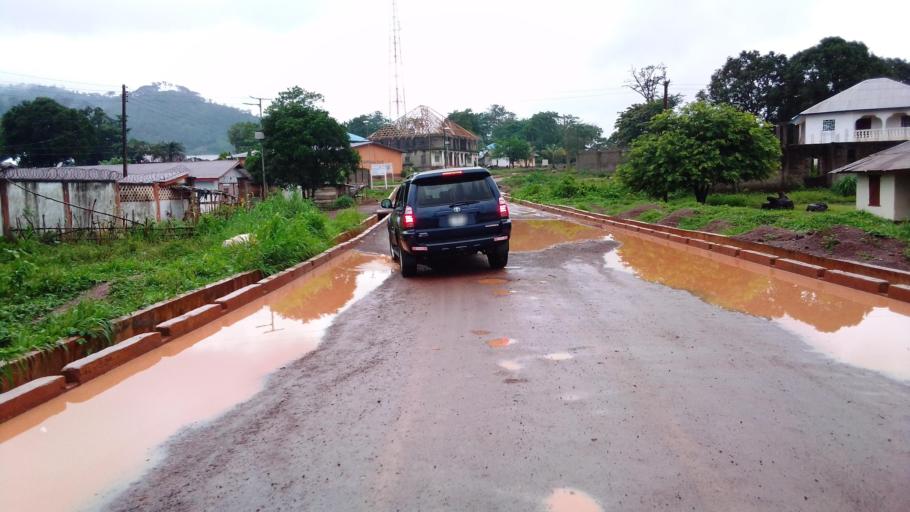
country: SL
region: Eastern Province
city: Kenema
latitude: 7.8853
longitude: -11.1930
